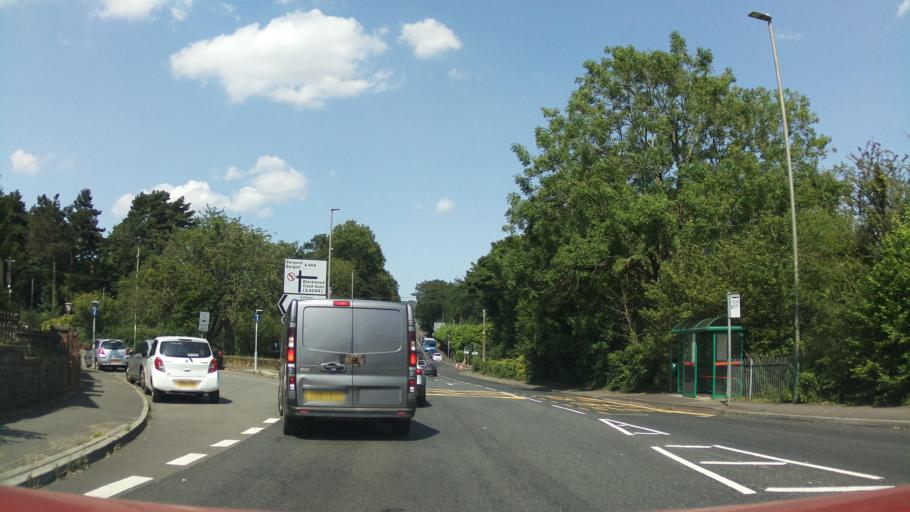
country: GB
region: Wales
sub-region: Caerphilly County Borough
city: Pengam
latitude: 51.6699
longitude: -3.2271
